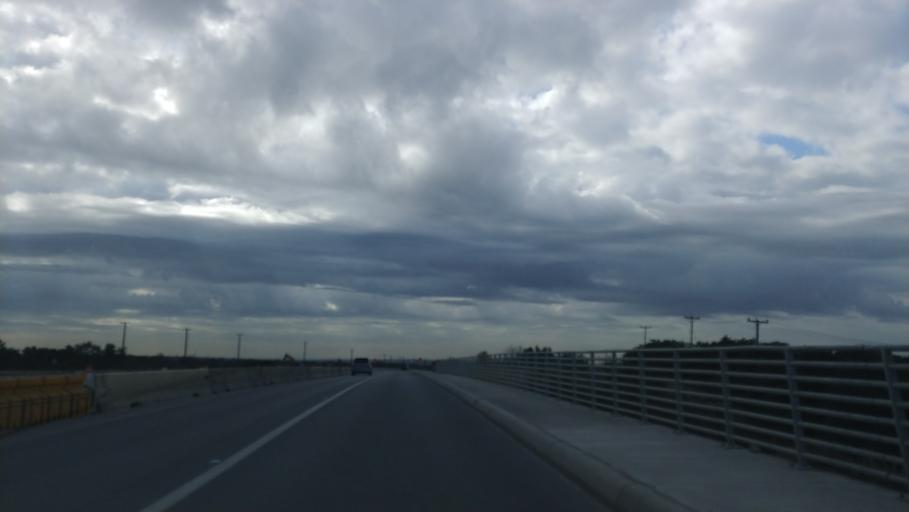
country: US
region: Texas
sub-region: Bexar County
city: Leon Valley
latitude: 29.4578
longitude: -98.7117
